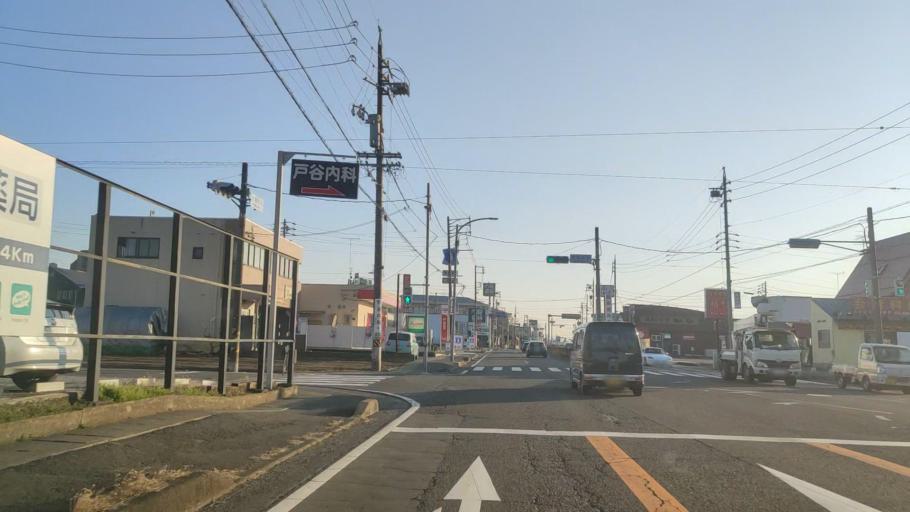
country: JP
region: Gifu
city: Gifu-shi
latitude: 35.4380
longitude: 136.7379
